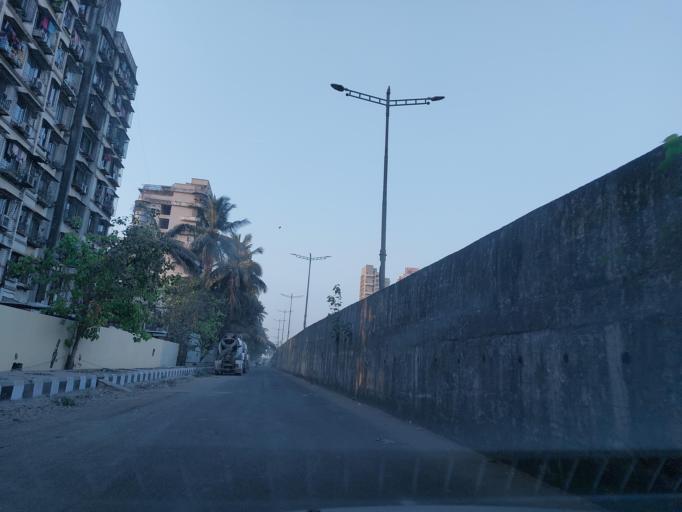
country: IN
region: Maharashtra
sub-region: Mumbai Suburban
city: Powai
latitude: 19.1114
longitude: 72.9327
